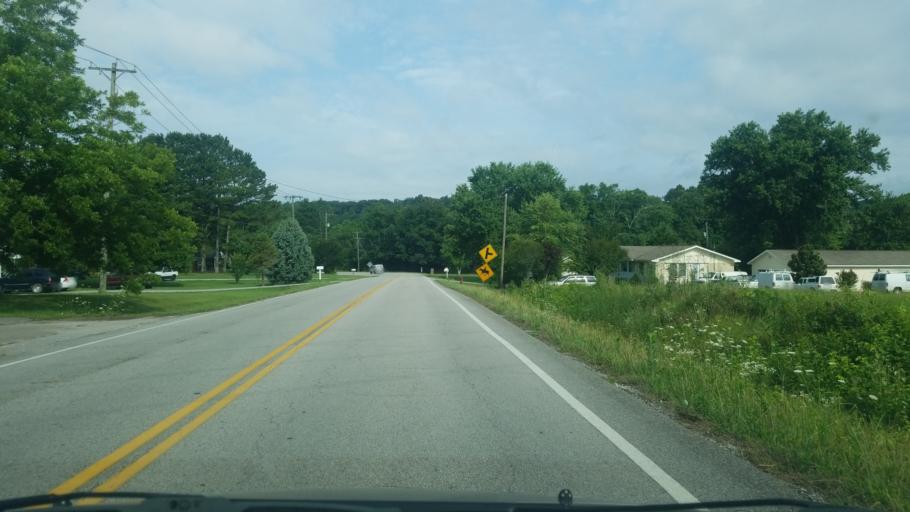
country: US
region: Tennessee
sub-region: Hamilton County
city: Apison
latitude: 35.0165
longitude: -85.0298
